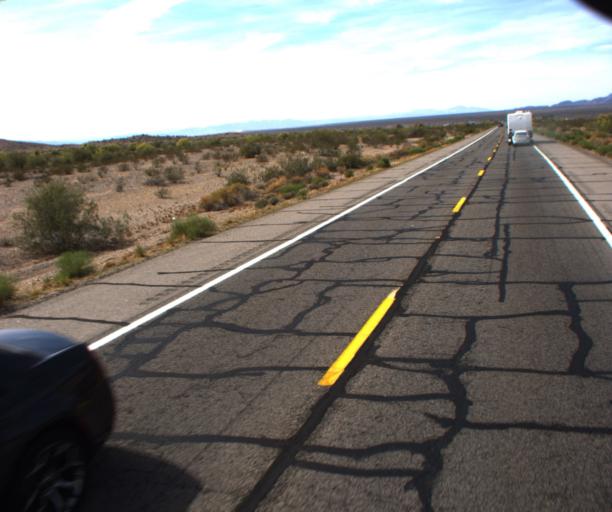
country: US
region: Arizona
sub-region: Mohave County
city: Desert Hills
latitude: 34.7094
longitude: -114.3053
